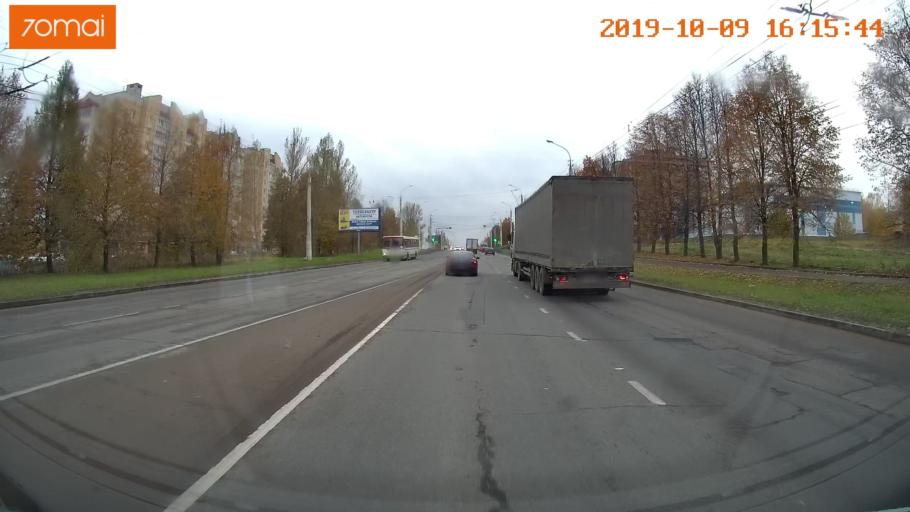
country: RU
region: Kostroma
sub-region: Kostromskoy Rayon
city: Kostroma
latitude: 57.7387
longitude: 40.9144
